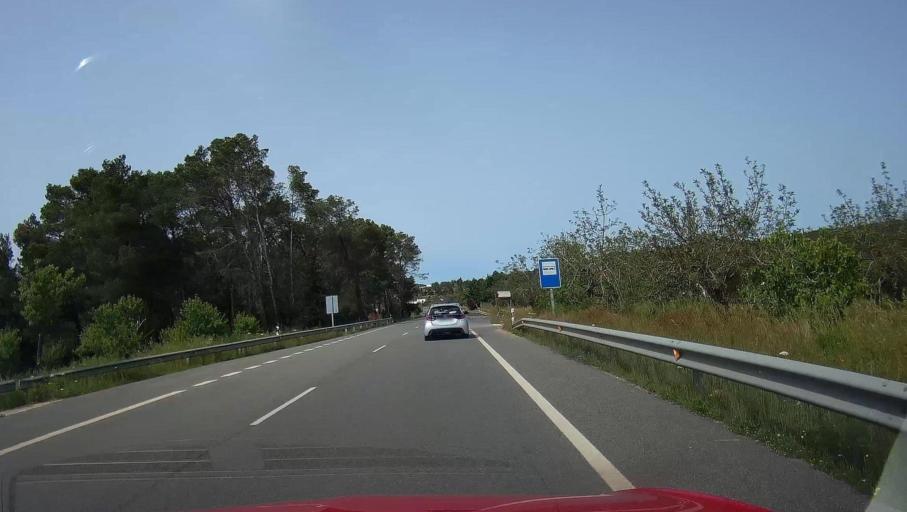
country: ES
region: Balearic Islands
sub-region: Illes Balears
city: Sant Joan de Labritja
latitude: 39.0587
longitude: 1.4941
